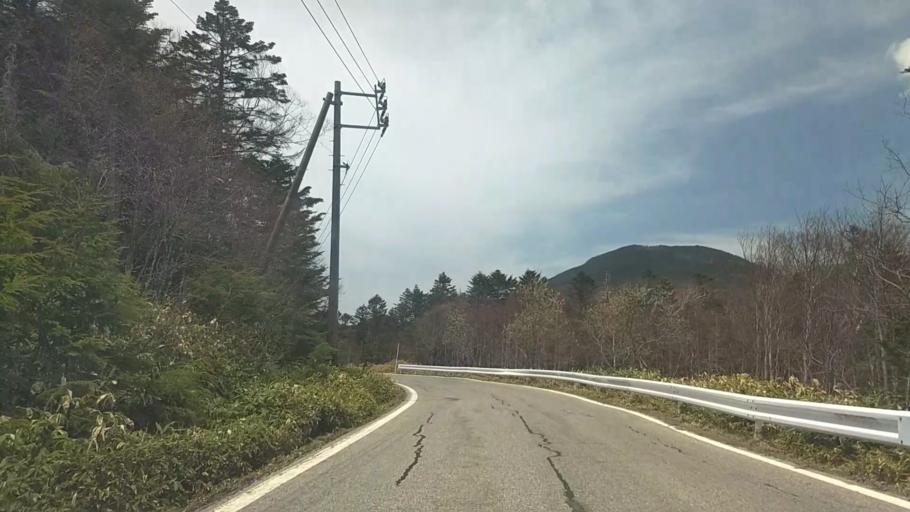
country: JP
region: Nagano
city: Saku
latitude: 36.0589
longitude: 138.3509
